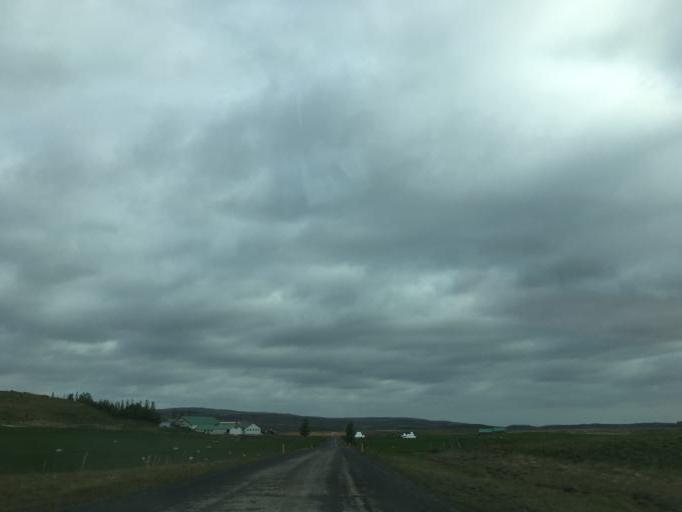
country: IS
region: South
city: Vestmannaeyjar
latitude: 64.2854
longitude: -20.2251
